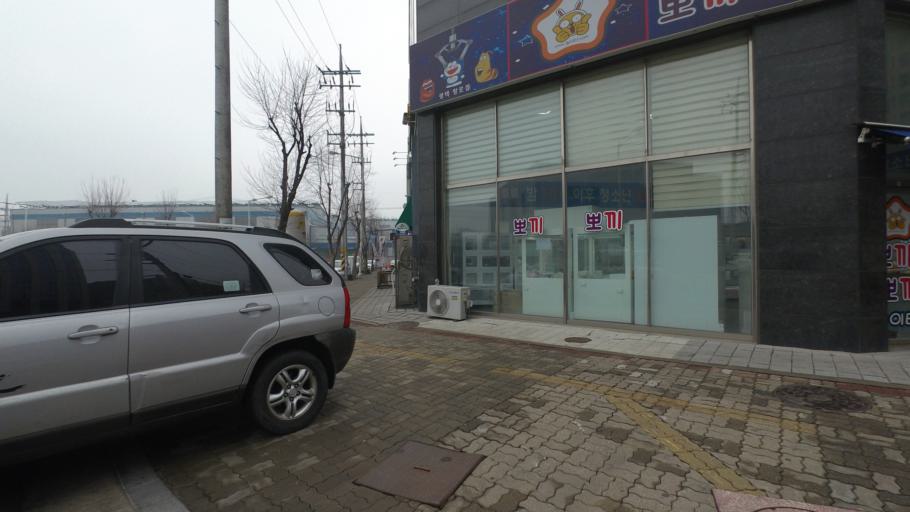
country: KR
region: Chungcheongnam-do
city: Tangjin
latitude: 36.9771
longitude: 126.8432
